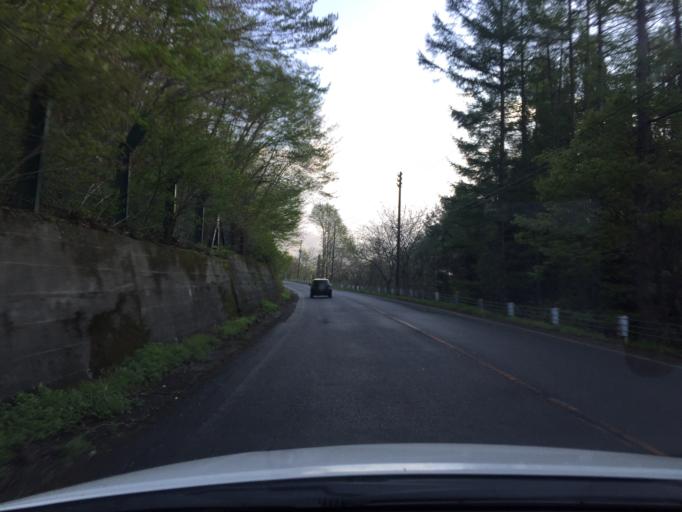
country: JP
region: Fukushima
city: Inawashiro
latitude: 37.6336
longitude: 140.1037
